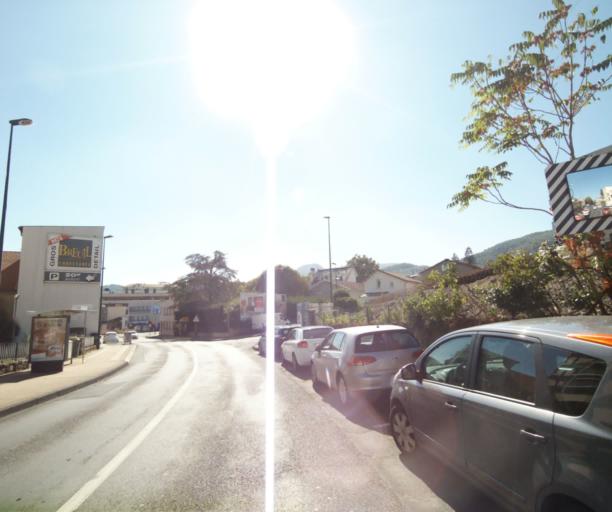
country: FR
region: Auvergne
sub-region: Departement du Puy-de-Dome
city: Chamalieres
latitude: 45.7796
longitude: 3.0623
